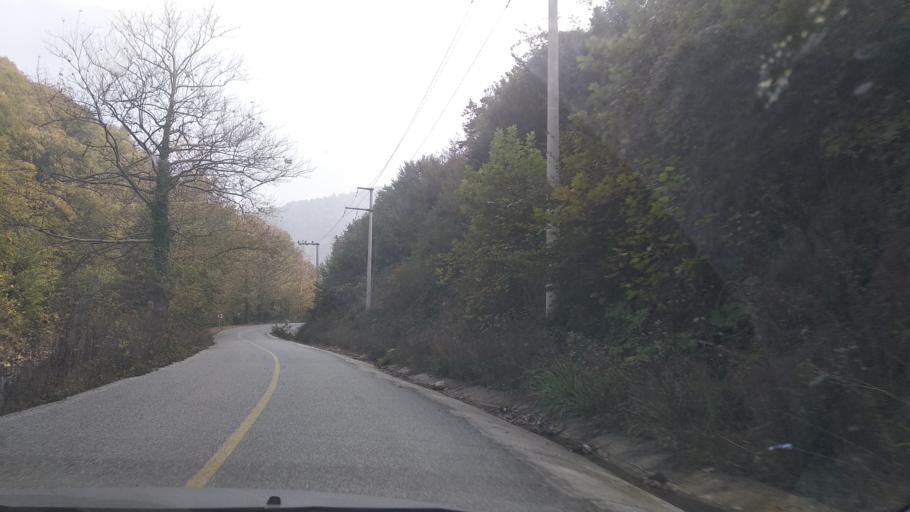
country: TR
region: Duzce
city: Kaynasli
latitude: 40.7305
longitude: 31.2305
